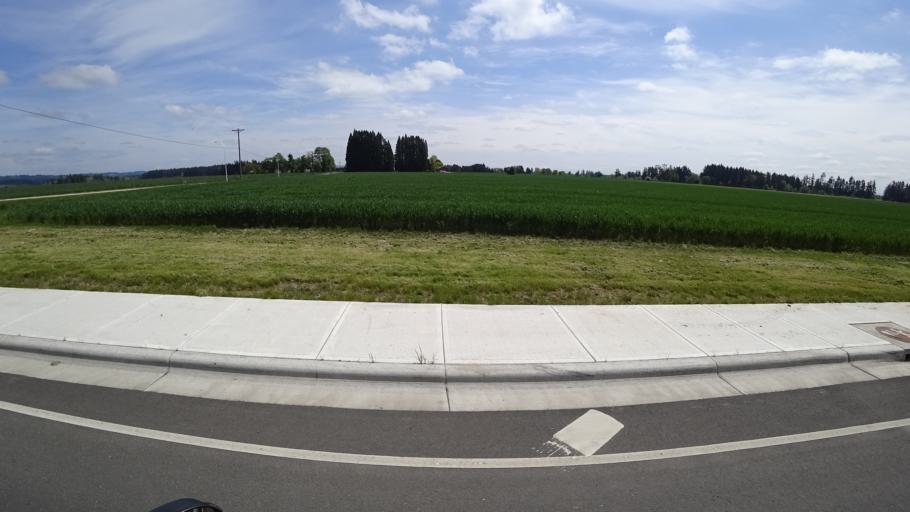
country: US
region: Oregon
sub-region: Washington County
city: North Plains
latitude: 45.5720
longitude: -122.9699
